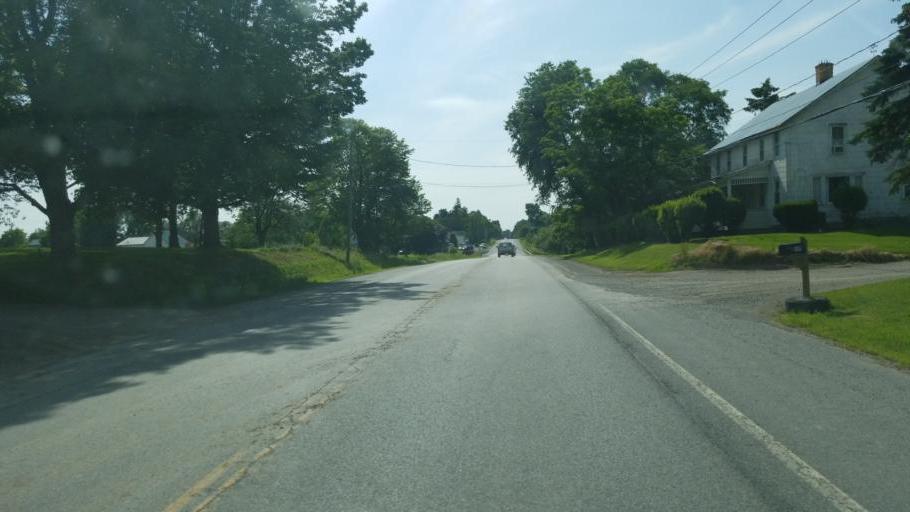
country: US
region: New York
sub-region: Monroe County
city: Honeoye Falls
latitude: 42.9047
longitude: -77.5225
